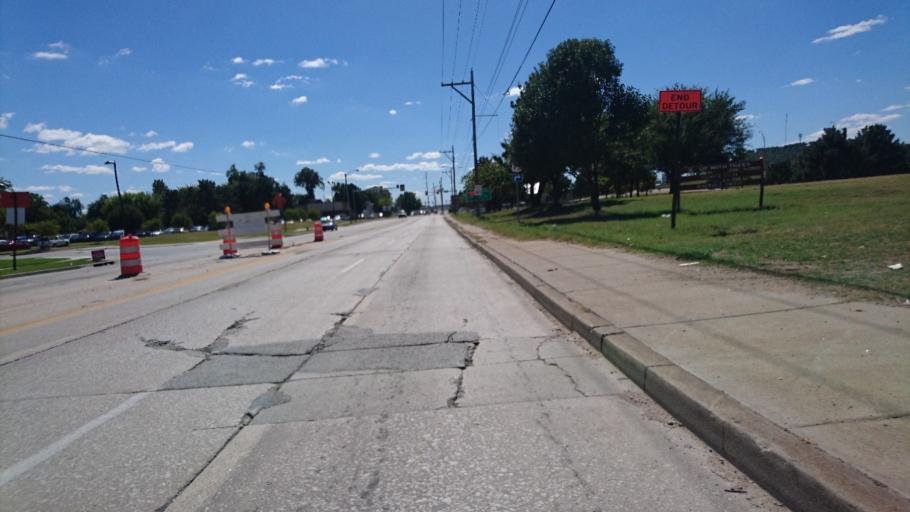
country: US
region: Oklahoma
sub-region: Tulsa County
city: Tulsa
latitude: 36.1295
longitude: -96.0071
